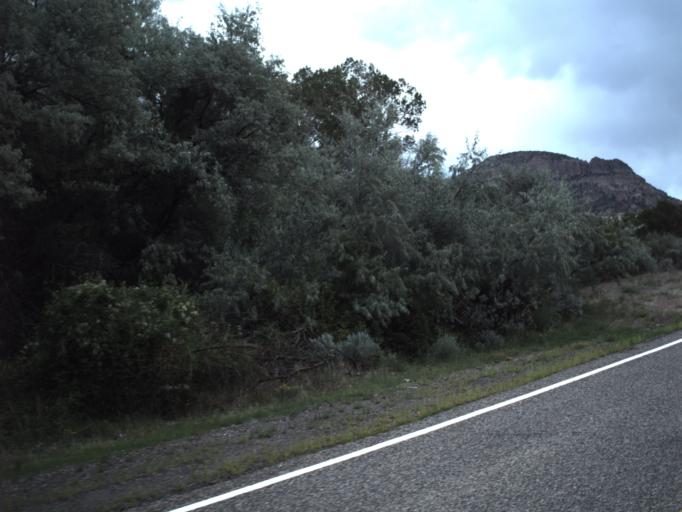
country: US
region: Utah
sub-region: Piute County
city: Junction
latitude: 38.2022
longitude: -112.1763
